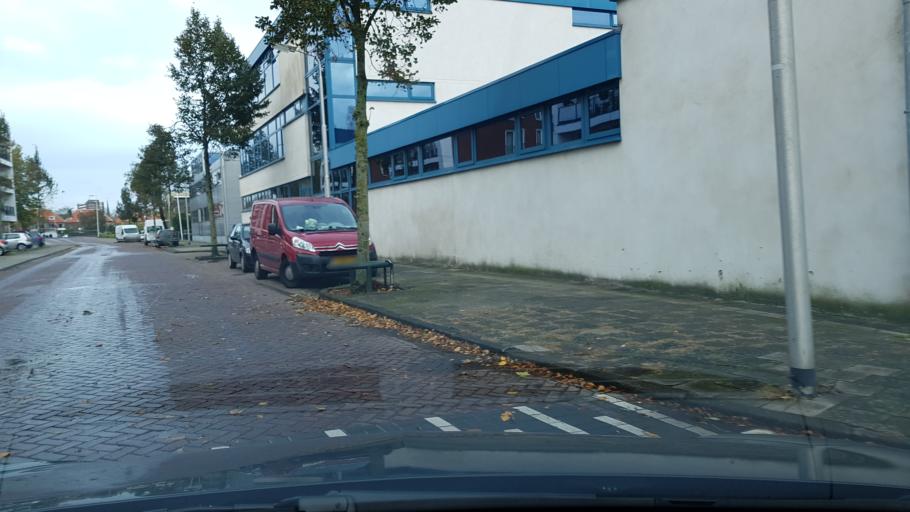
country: NL
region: North Holland
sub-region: Gemeente Heemstede
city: Heemstede
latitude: 52.3462
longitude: 4.6275
